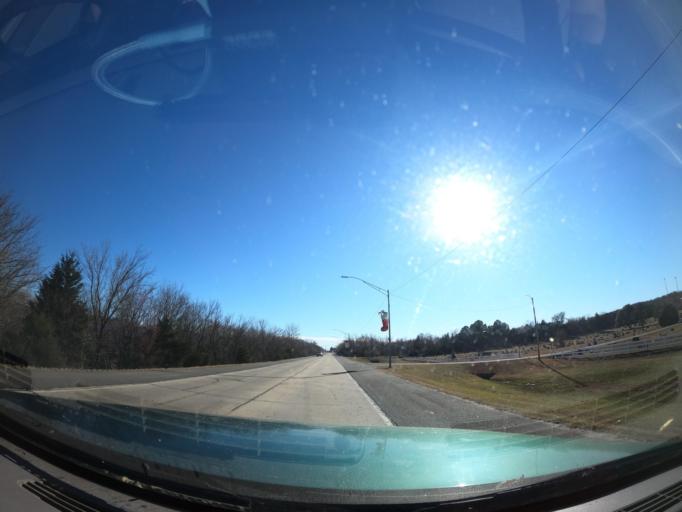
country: US
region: Oklahoma
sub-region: McIntosh County
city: Eufaula
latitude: 35.2949
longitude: -95.5823
